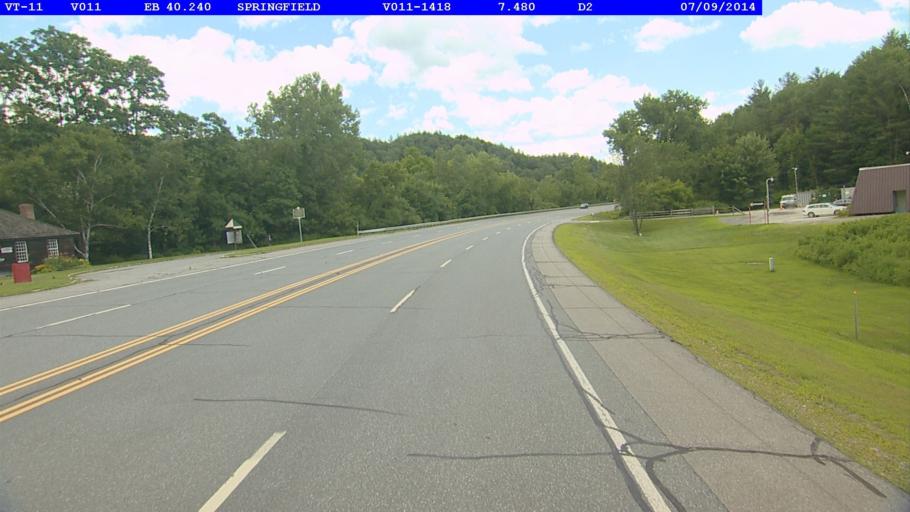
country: US
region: New Hampshire
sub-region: Sullivan County
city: Charlestown
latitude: 43.2699
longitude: -72.4485
